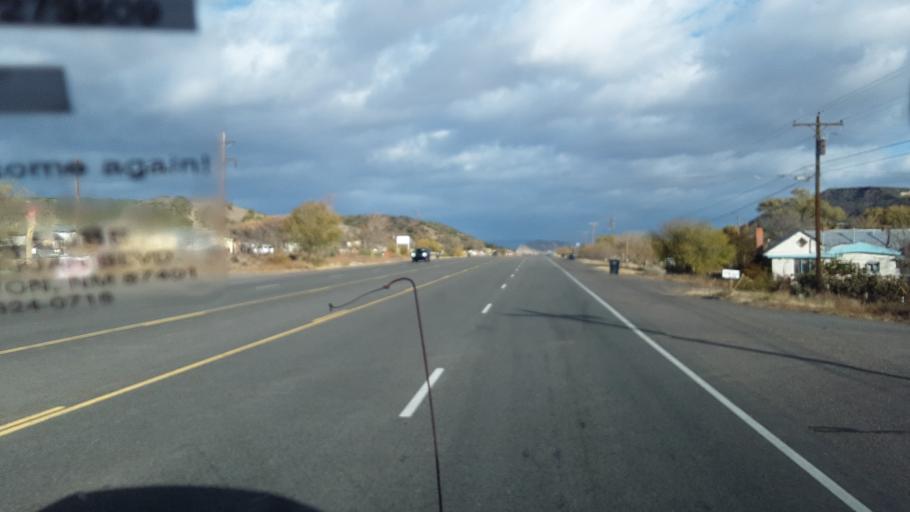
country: US
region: New Mexico
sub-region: Rio Arriba County
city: Ohkay Owingeh
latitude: 36.0651
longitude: -106.1211
